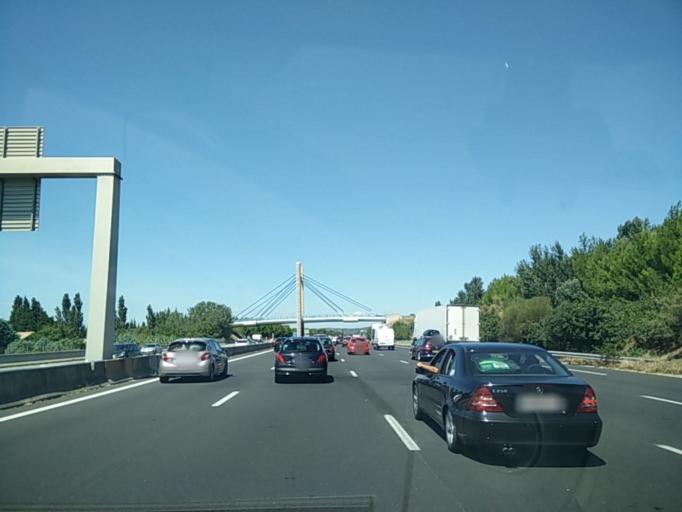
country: FR
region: Provence-Alpes-Cote d'Azur
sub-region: Departement du Vaucluse
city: Orange
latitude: 44.1428
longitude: 4.7778
